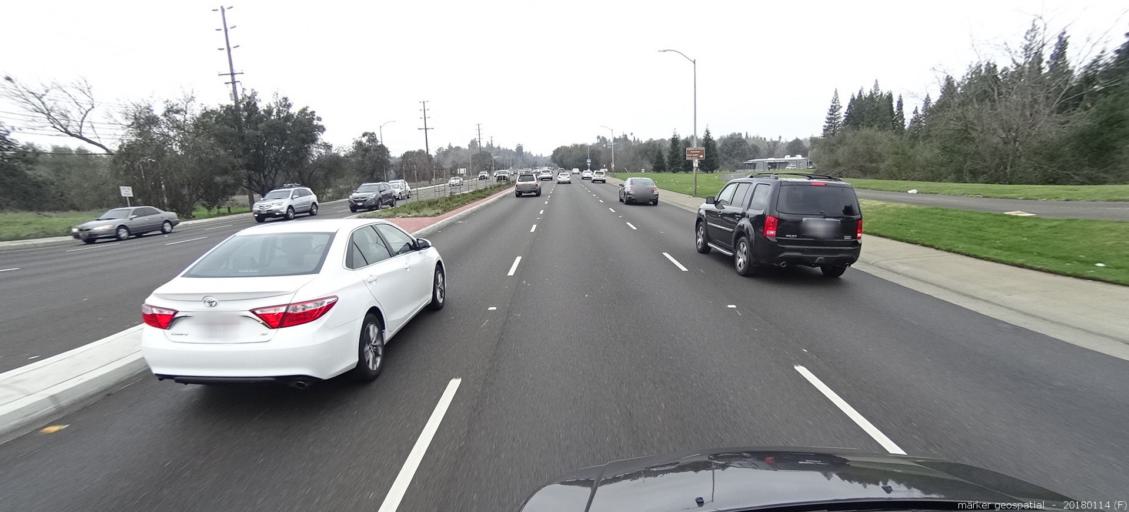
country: US
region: California
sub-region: Sacramento County
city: Fair Oaks
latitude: 38.6290
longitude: -121.2664
